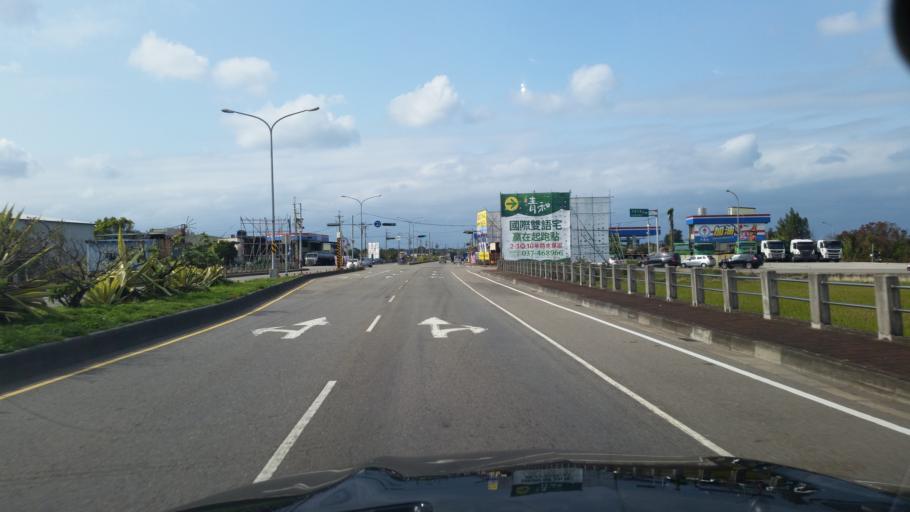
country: TW
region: Taiwan
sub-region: Miaoli
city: Miaoli
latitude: 24.6716
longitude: 120.8562
